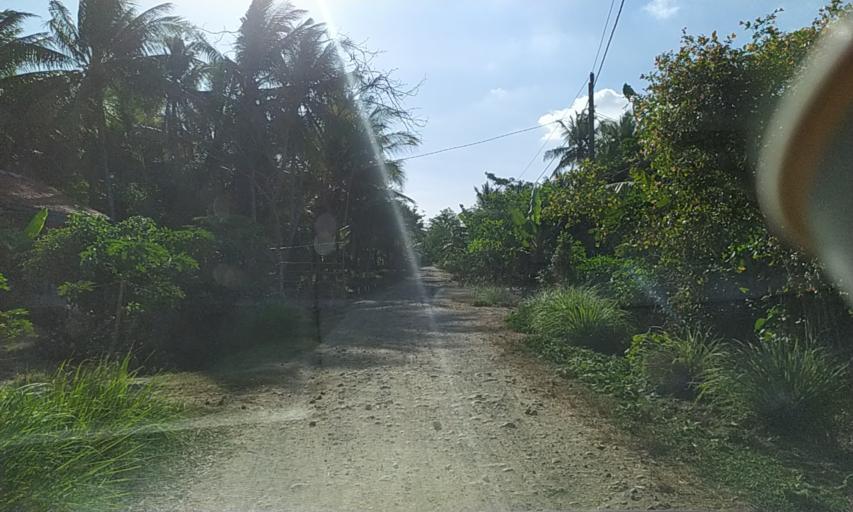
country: ID
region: Central Java
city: Kalenaren
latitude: -7.5942
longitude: 108.8068
